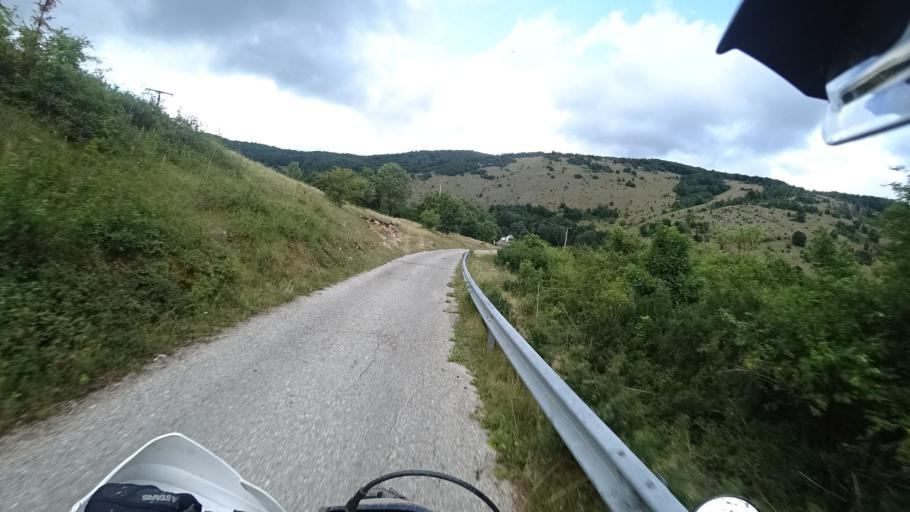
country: HR
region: Licko-Senjska
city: Jezerce
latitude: 44.7379
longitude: 15.4933
